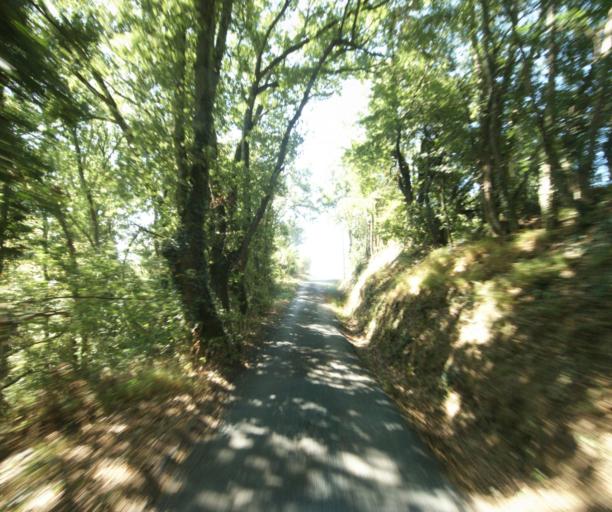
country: FR
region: Rhone-Alpes
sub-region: Departement du Rhone
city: Savigny
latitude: 45.8176
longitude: 4.5569
